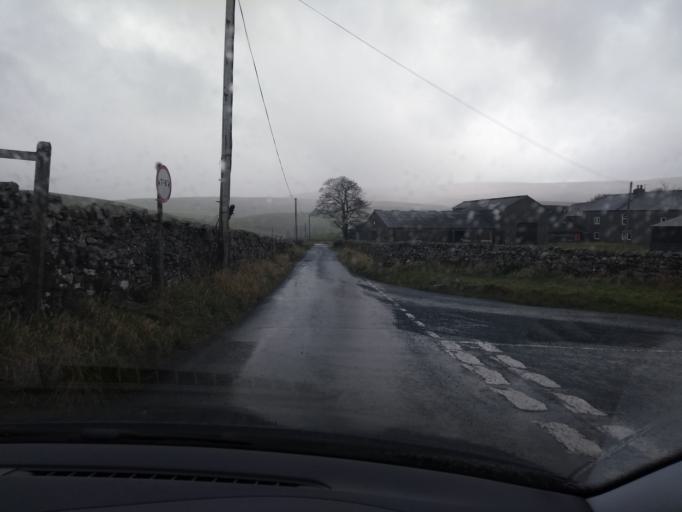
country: GB
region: England
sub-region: North Yorkshire
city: Settle
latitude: 54.1138
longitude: -2.2544
